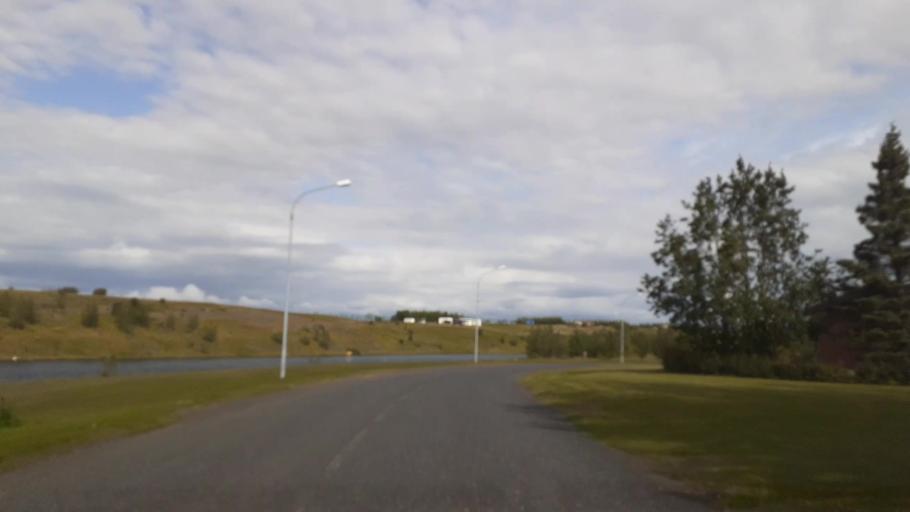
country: IS
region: South
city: Vestmannaeyjar
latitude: 63.8409
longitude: -20.4002
